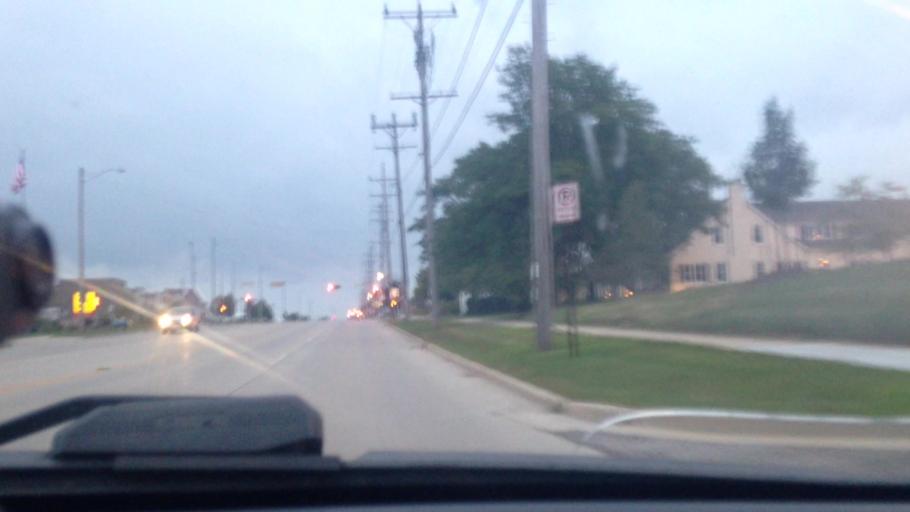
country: US
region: Wisconsin
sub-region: Washington County
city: West Bend
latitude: 43.4028
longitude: -88.1813
